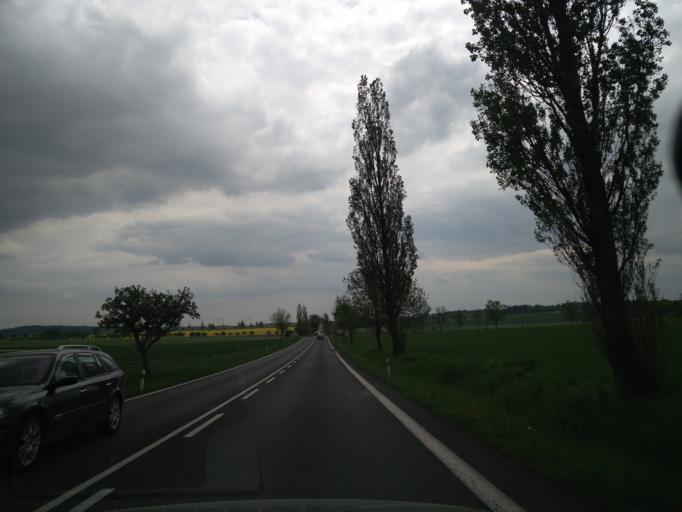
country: CZ
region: Central Bohemia
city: Milin
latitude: 49.6131
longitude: 14.0571
